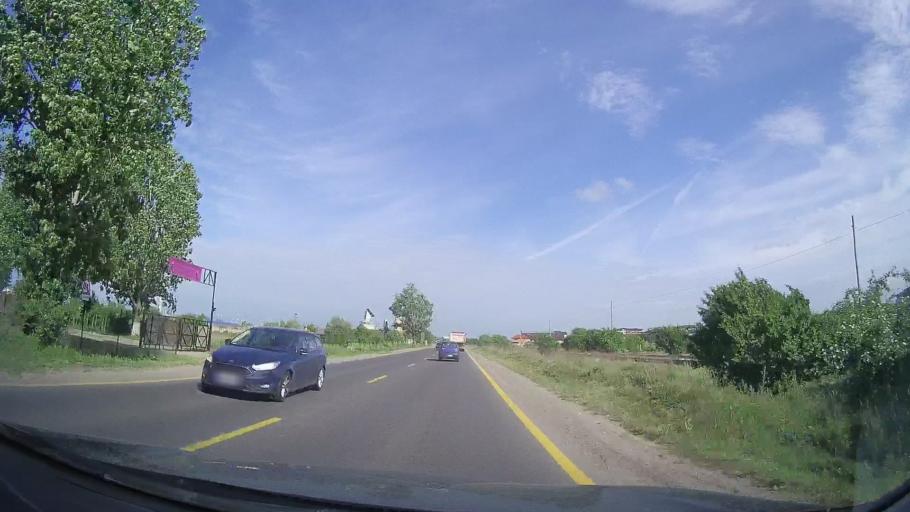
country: RO
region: Ilfov
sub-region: Comuna Magurele
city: Varteju
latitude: 44.3768
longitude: 26.0035
